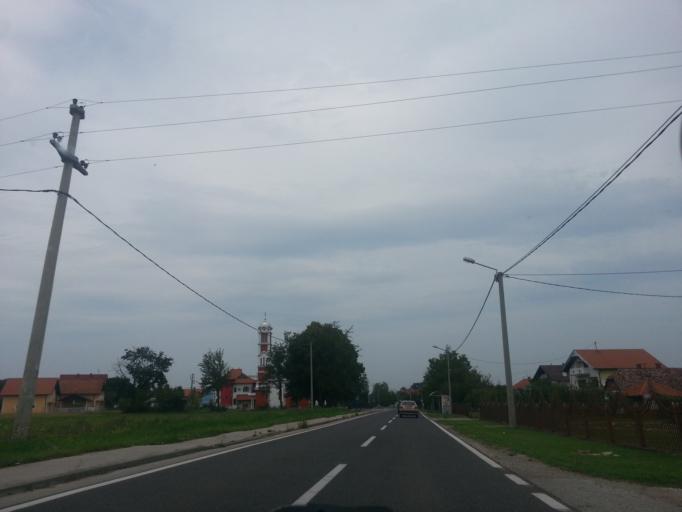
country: BA
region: Brcko
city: Brcko
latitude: 44.8322
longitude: 18.8198
